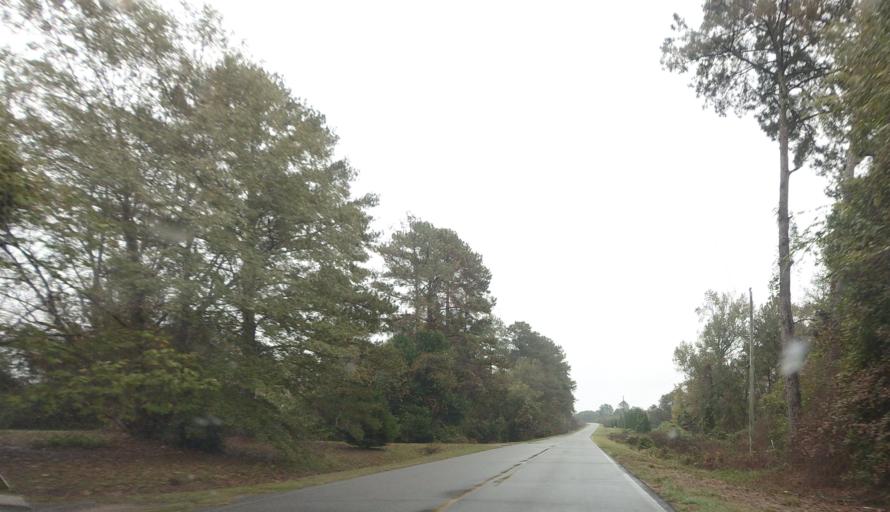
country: US
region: Georgia
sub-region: Macon County
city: Marshallville
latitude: 32.5268
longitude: -83.9795
